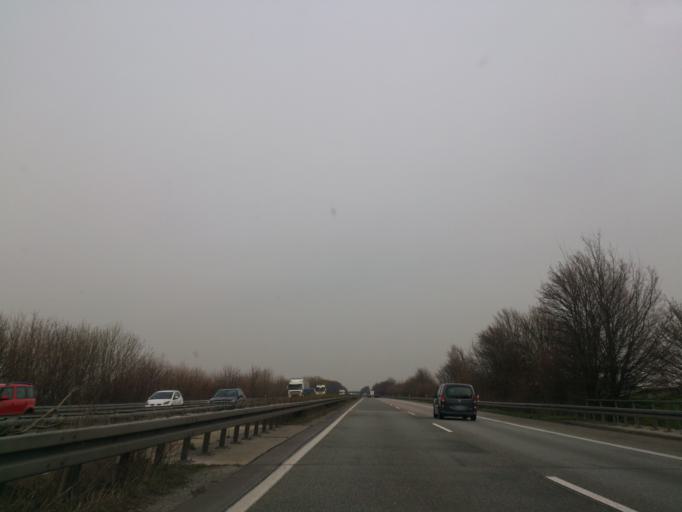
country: DE
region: North Rhine-Westphalia
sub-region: Regierungsbezirk Arnsberg
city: Anrochte
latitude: 51.5856
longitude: 8.3601
